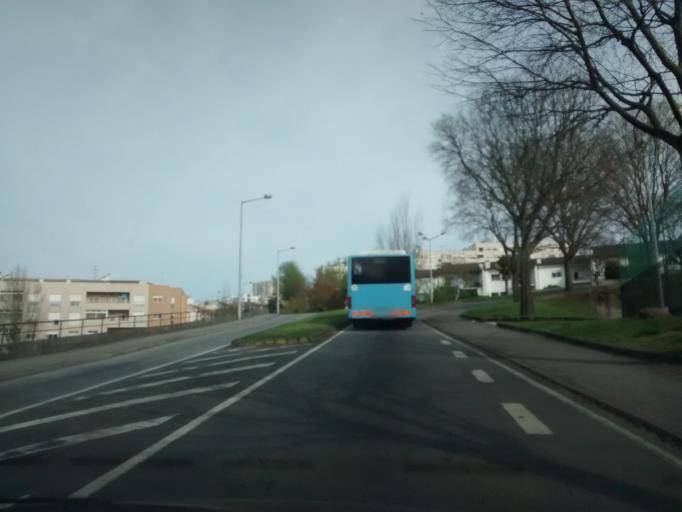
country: PT
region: Braga
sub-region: Braga
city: Braga
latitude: 41.5563
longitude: -8.4388
